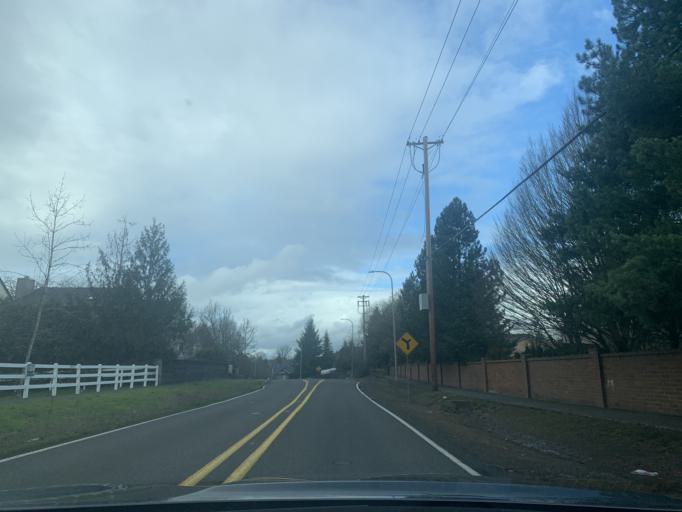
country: US
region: Oregon
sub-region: Washington County
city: Oak Hills
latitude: 45.5585
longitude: -122.8316
